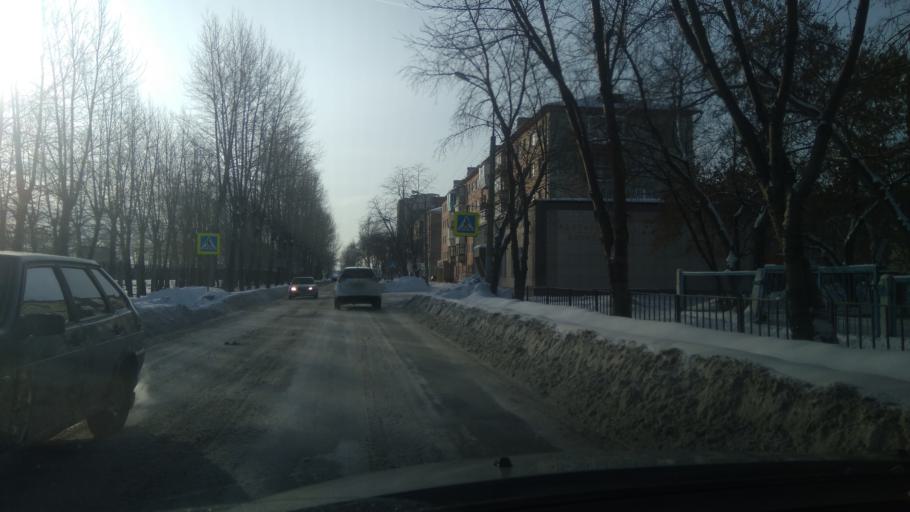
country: RU
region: Sverdlovsk
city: Sukhoy Log
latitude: 56.9019
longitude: 62.0302
